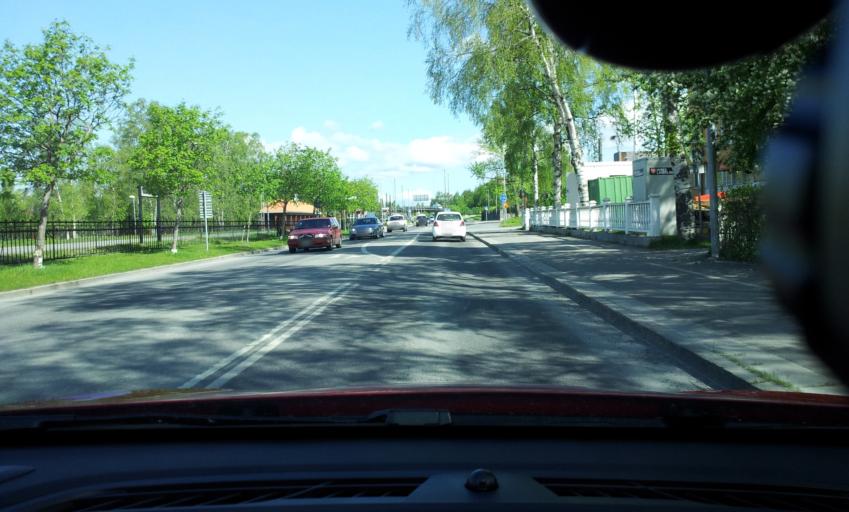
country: SE
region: Jaemtland
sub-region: OEstersunds Kommun
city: Ostersund
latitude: 63.1775
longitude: 14.6317
